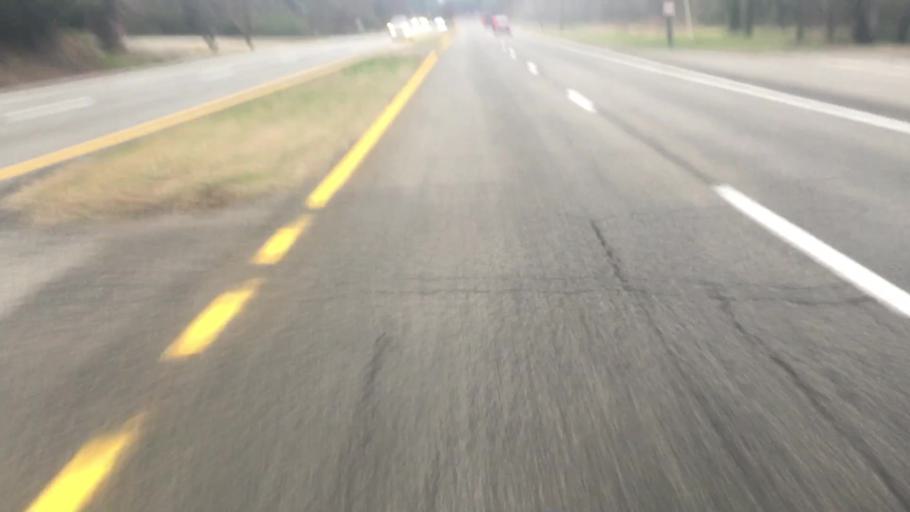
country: US
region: Alabama
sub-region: Jefferson County
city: Fultondale
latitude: 33.5745
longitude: -86.8080
